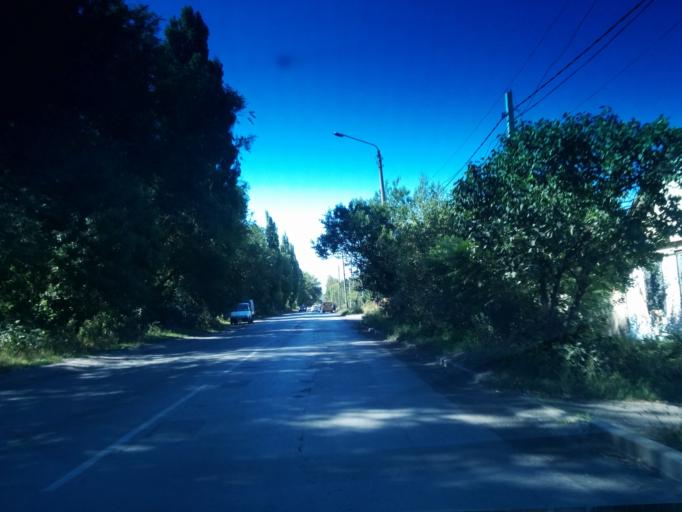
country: RU
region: Rostov
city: Shakhty
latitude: 47.6801
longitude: 40.2814
